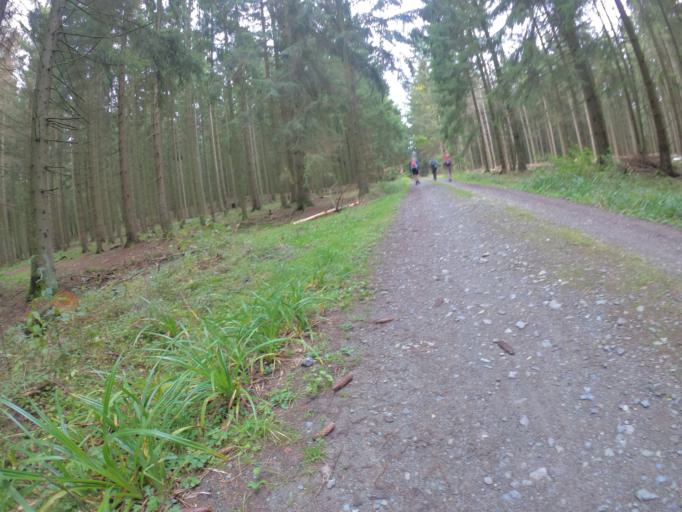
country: DE
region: Hesse
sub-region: Regierungsbezirk Darmstadt
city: Niedernhausen
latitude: 50.1878
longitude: 8.3228
